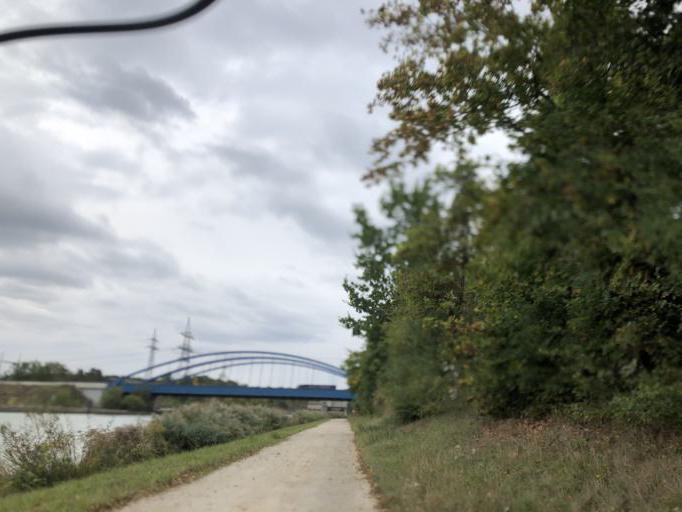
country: DE
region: Bavaria
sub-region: Regierungsbezirk Mittelfranken
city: Erlangen
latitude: 49.5622
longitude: 10.9699
